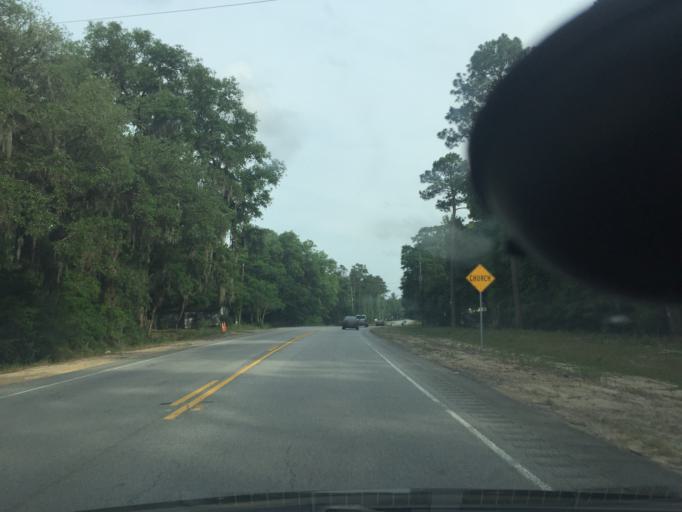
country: US
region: Georgia
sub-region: Chatham County
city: Bloomingdale
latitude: 32.0376
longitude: -81.3274
